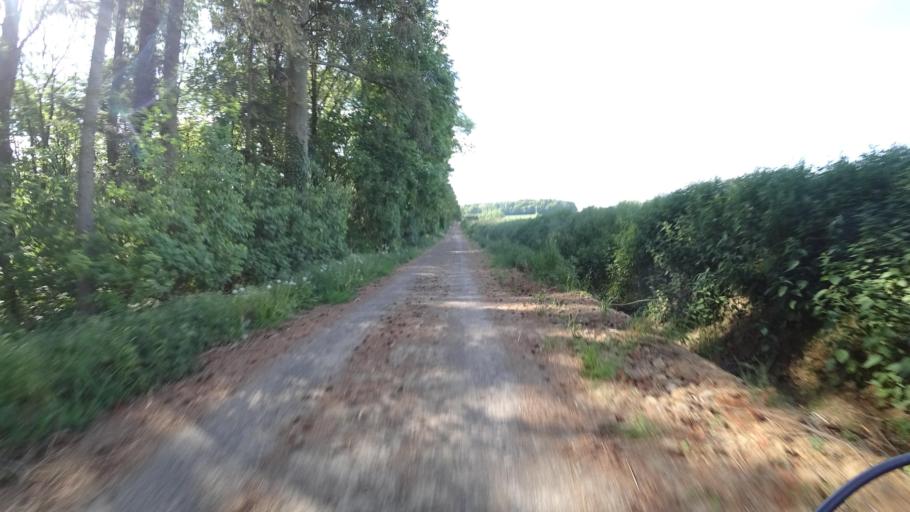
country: BE
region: Wallonia
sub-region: Province de Namur
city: Namur
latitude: 50.4988
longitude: 4.8208
